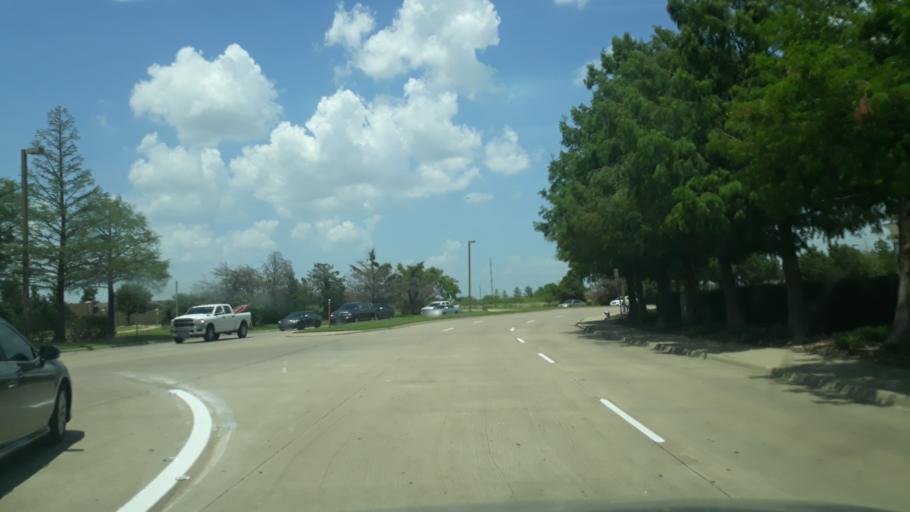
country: US
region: Texas
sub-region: Dallas County
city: Coppell
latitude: 32.9692
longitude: -97.0389
